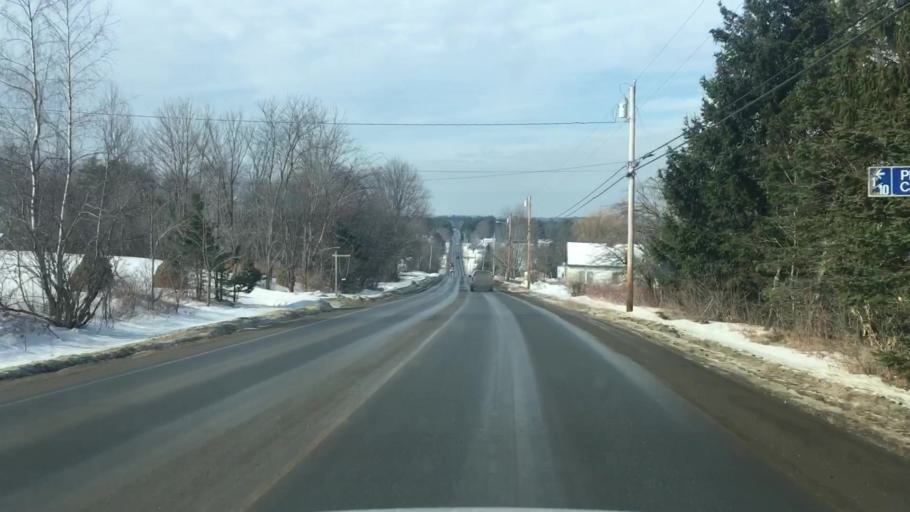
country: US
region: Maine
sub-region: Penobscot County
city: Hermon
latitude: 44.8483
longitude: -68.8741
